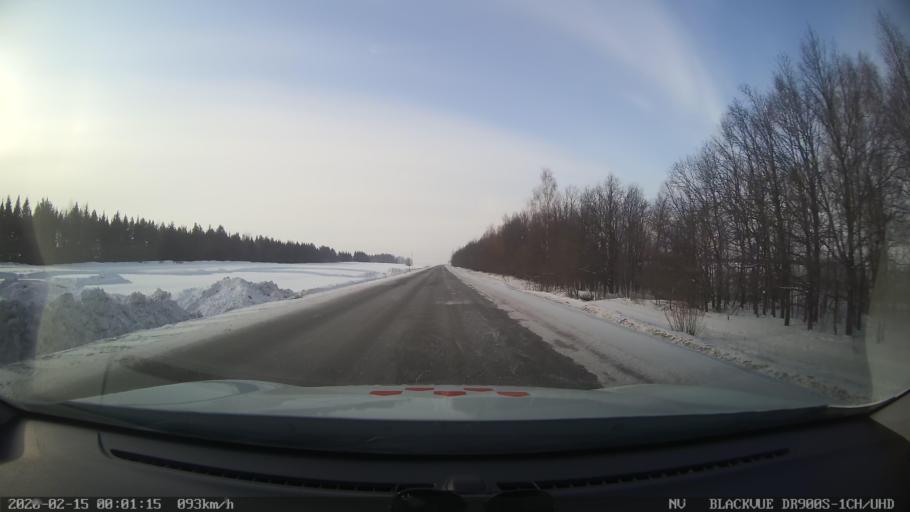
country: RU
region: Tatarstan
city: Kuybyshevskiy Zaton
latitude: 55.3452
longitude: 49.0251
